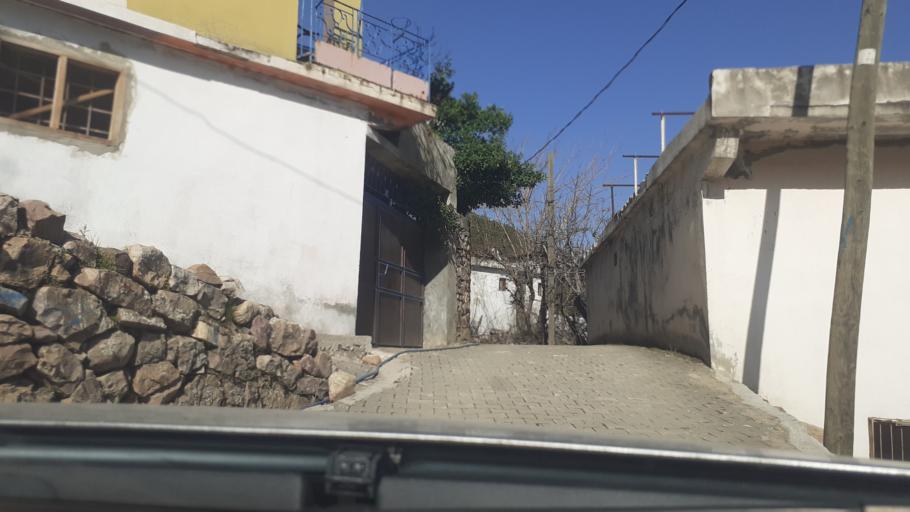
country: TR
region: Hatay
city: Aktepe
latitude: 36.7586
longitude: 36.4487
